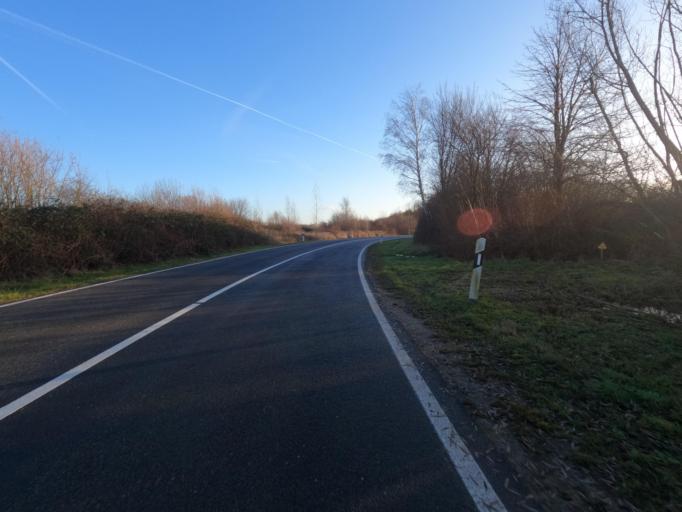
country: DE
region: North Rhine-Westphalia
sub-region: Regierungsbezirk Koln
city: Elsdorf
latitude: 50.9370
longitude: 6.5218
